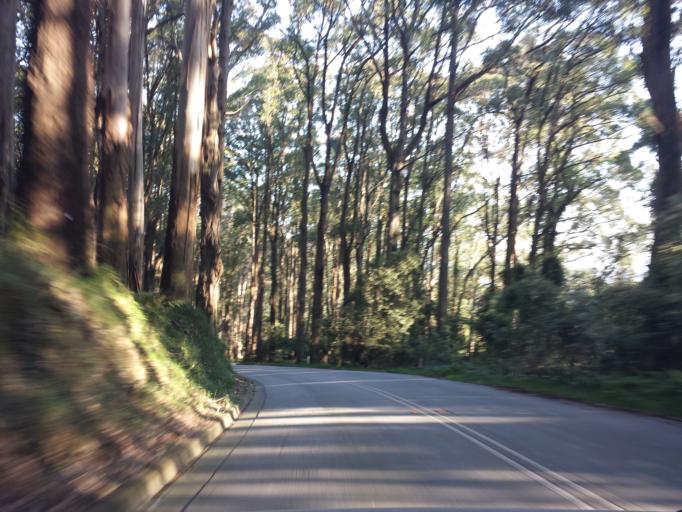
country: AU
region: Victoria
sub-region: Yarra Ranges
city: Belgrave
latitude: -37.8898
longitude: 145.3456
